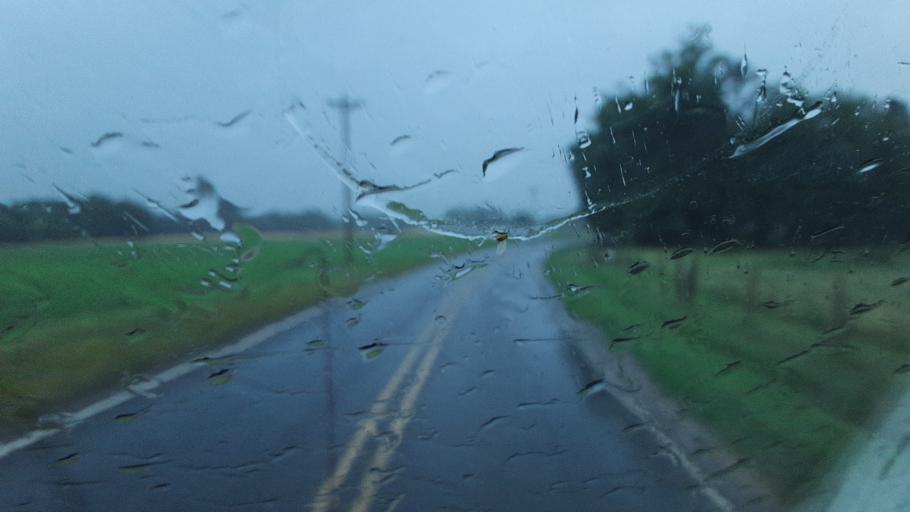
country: US
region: North Carolina
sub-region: Yadkin County
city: Jonesville
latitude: 36.0973
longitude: -80.8631
